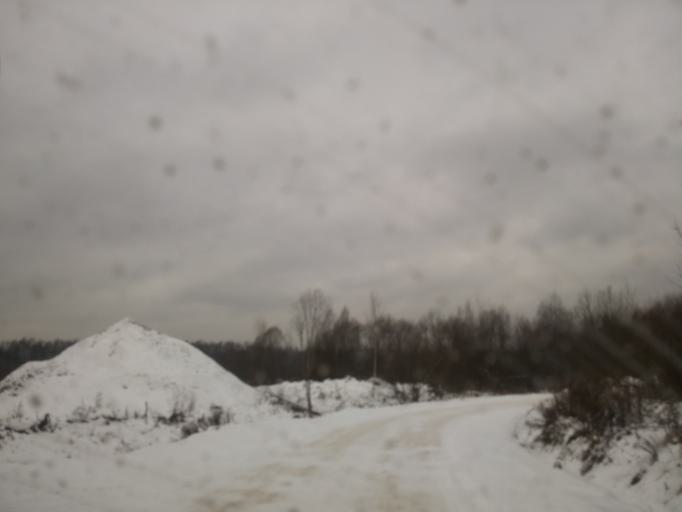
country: RU
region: Moskovskaya
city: Reshetnikovo
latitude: 56.4582
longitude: 36.5459
